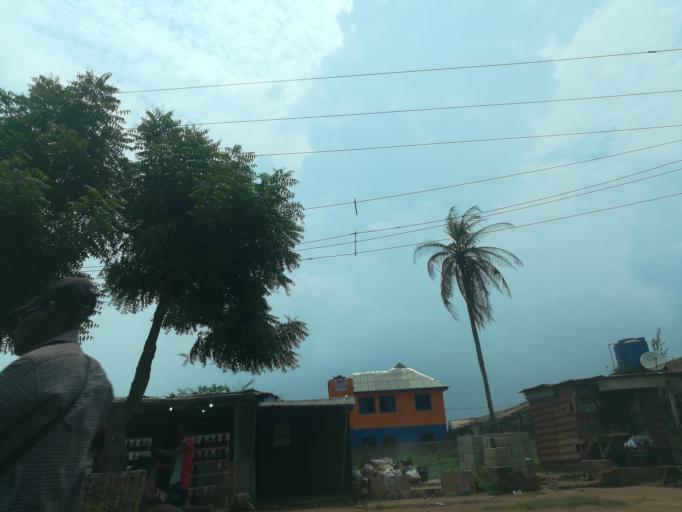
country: NG
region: Lagos
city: Ikorodu
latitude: 6.5968
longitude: 3.5886
